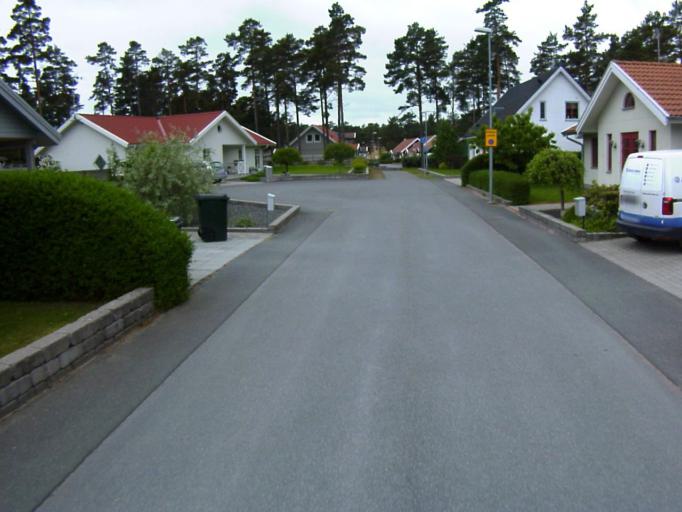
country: SE
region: Skane
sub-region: Kristianstads Kommun
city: Ahus
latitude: 55.9429
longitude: 14.3014
